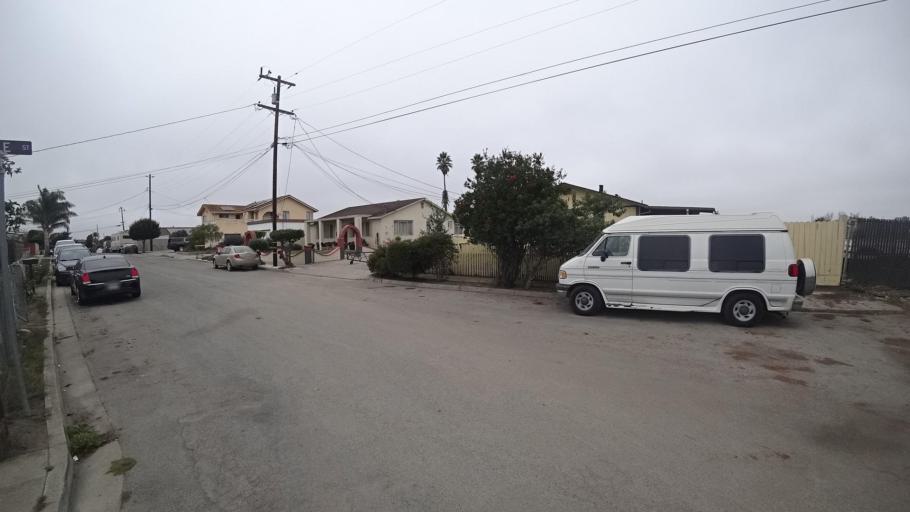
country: US
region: California
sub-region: Monterey County
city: Castroville
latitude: 36.7686
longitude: -121.7504
